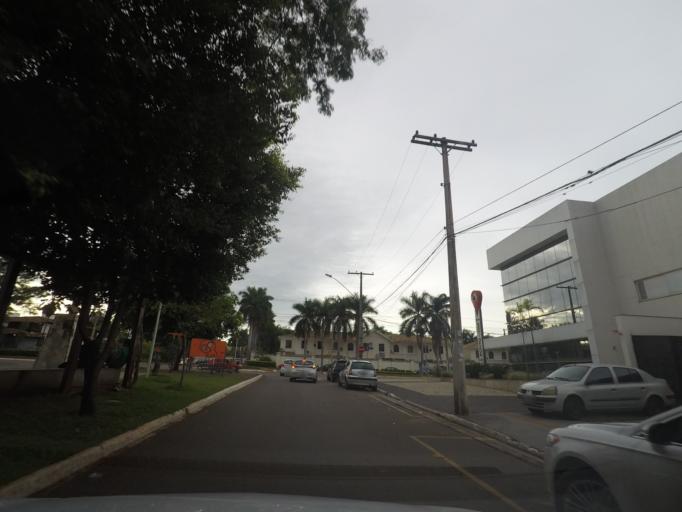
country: BR
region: Goias
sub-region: Goiania
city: Goiania
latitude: -16.7027
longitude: -49.2575
